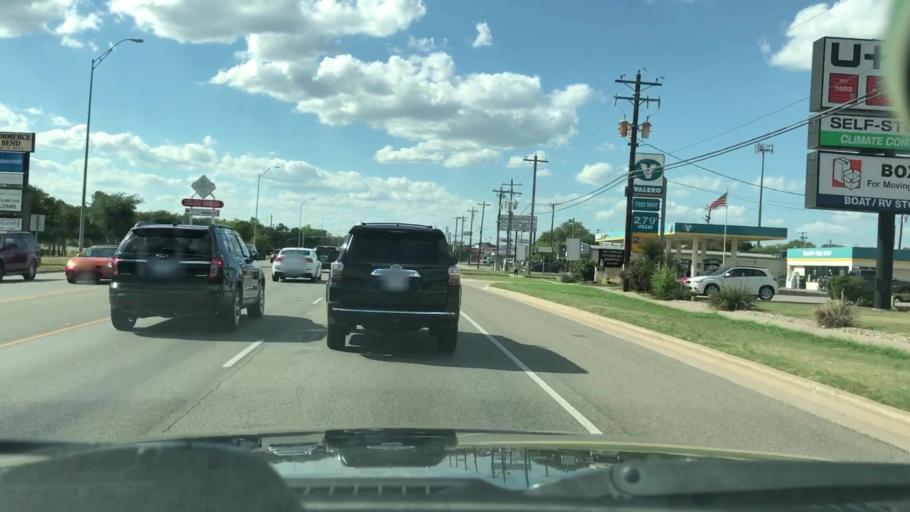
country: US
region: Texas
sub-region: Williamson County
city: Cedar Park
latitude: 30.5028
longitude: -97.8179
